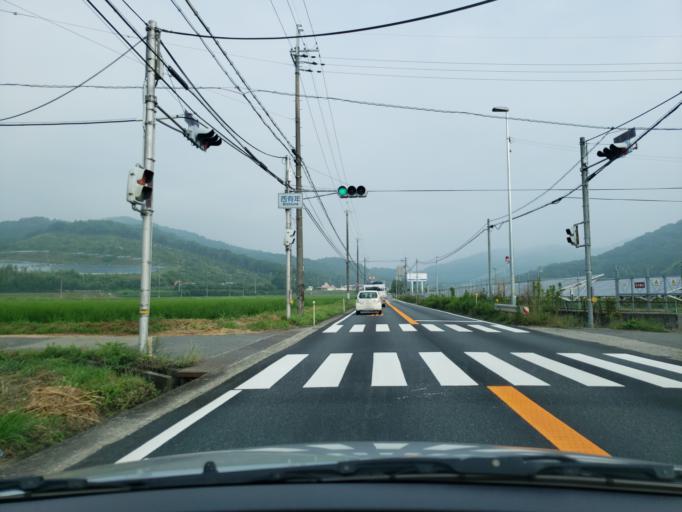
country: JP
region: Hyogo
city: Kariya
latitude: 34.8343
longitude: 134.3492
